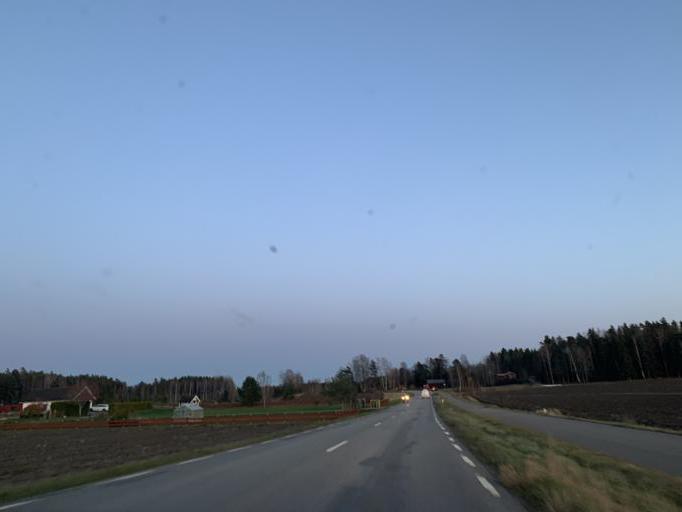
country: SE
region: OErebro
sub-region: Lindesbergs Kommun
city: Frovi
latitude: 59.3262
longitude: 15.4401
